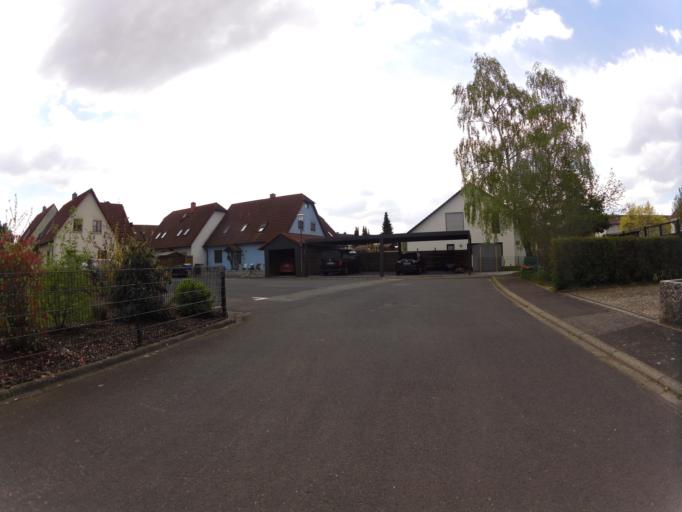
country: DE
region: Bavaria
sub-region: Regierungsbezirk Unterfranken
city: Giebelstadt
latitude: 49.6543
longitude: 9.9408
